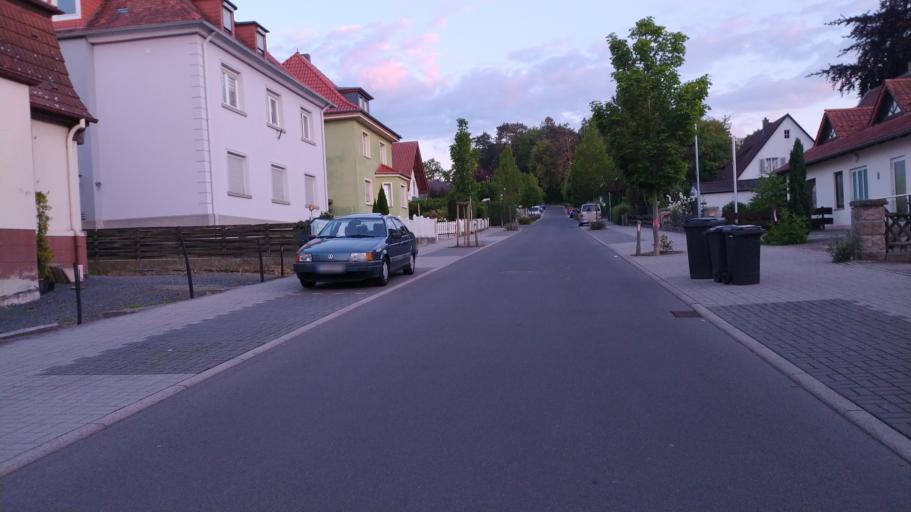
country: DE
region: Hesse
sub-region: Regierungsbezirk Kassel
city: Hunfeld
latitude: 50.6687
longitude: 9.7653
